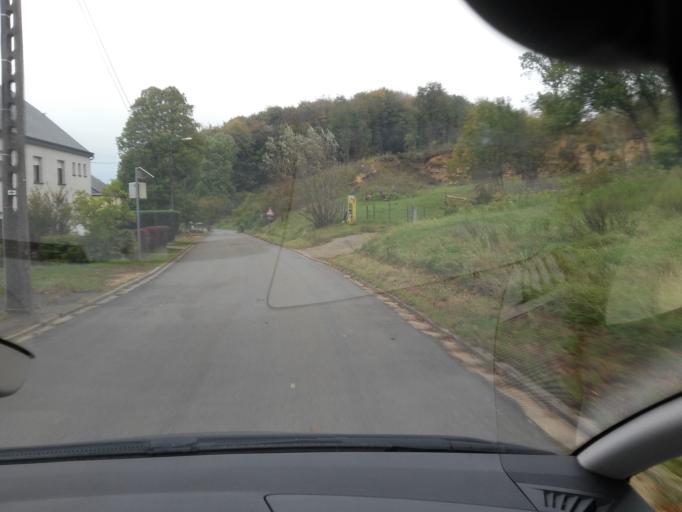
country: BE
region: Wallonia
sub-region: Province du Luxembourg
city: Attert
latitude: 49.7141
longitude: 5.7390
